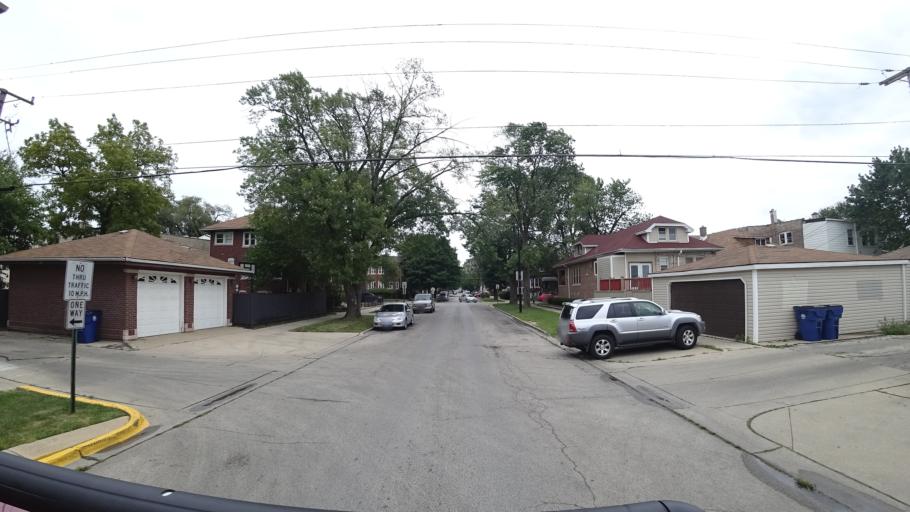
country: US
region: Illinois
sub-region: Cook County
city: Cicero
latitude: 41.8637
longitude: -87.7711
